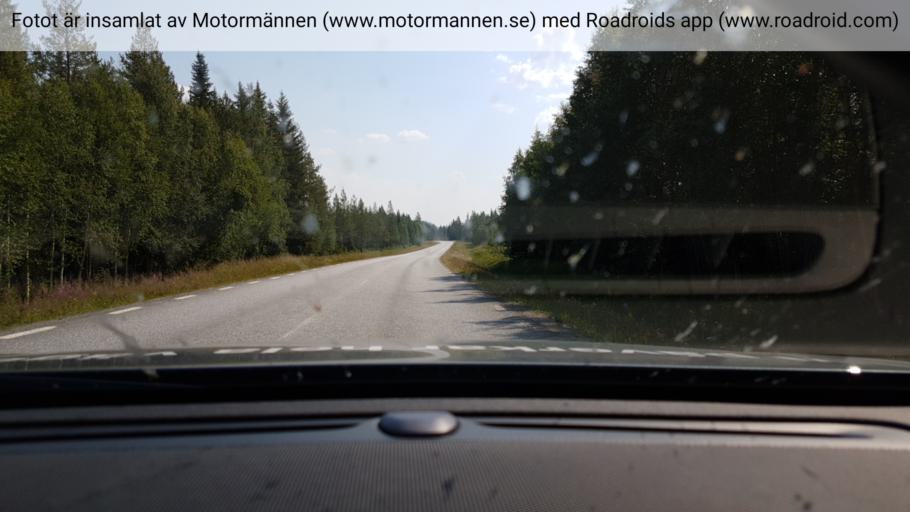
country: SE
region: Vaesterbotten
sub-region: Storumans Kommun
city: Fristad
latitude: 65.3935
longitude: 16.4548
